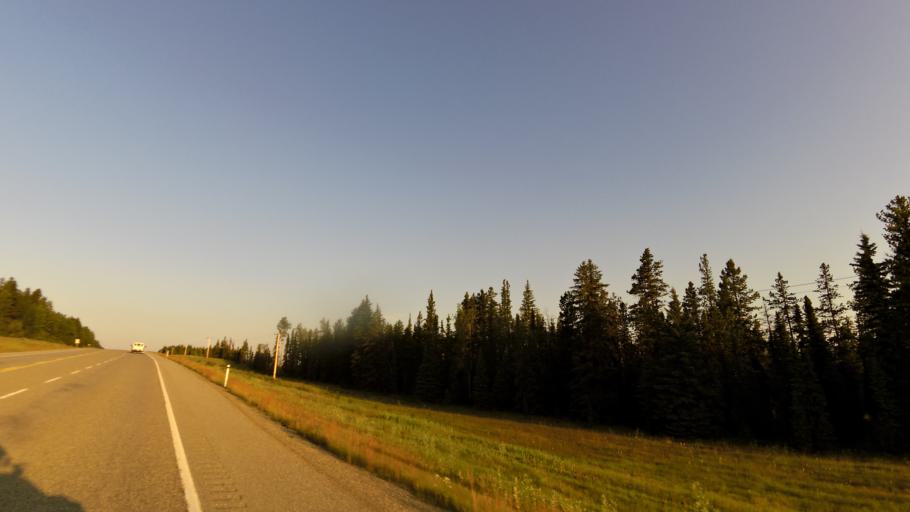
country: CA
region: Alberta
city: Rocky Mountain House
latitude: 52.4760
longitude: -115.6483
